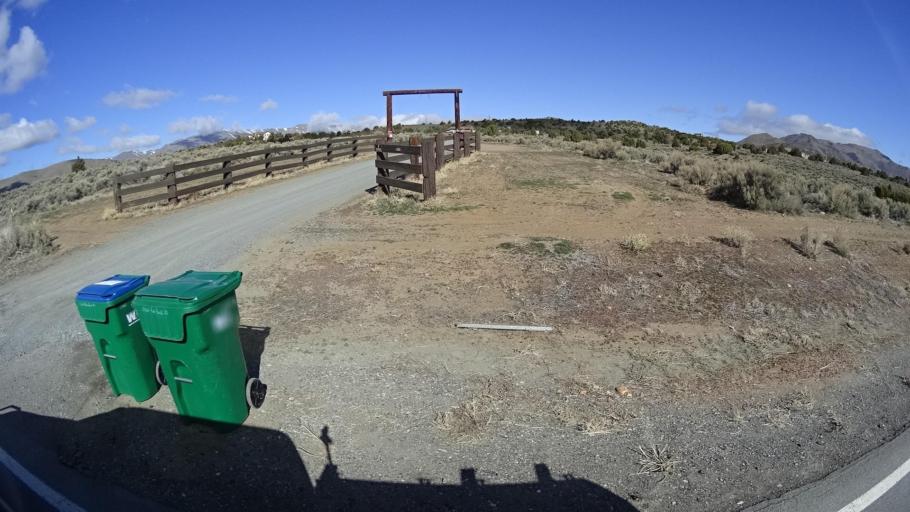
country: US
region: Nevada
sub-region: Washoe County
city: Lemmon Valley
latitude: 39.7196
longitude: -119.8840
